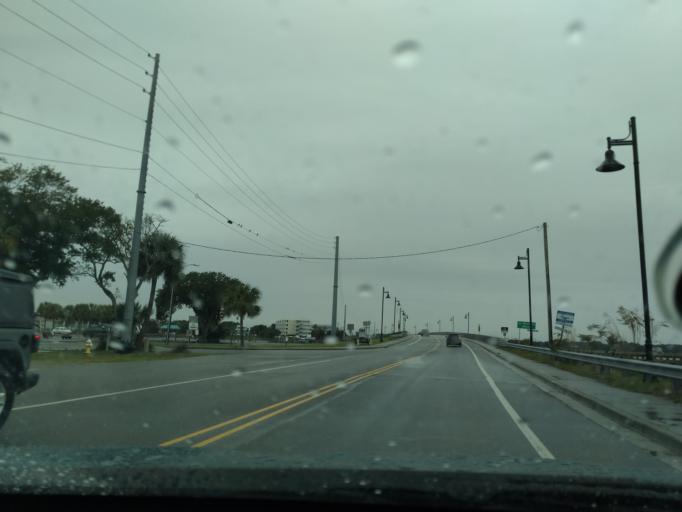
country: US
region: South Carolina
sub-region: Charleston County
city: Folly Beach
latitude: 32.6590
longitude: -79.9426
